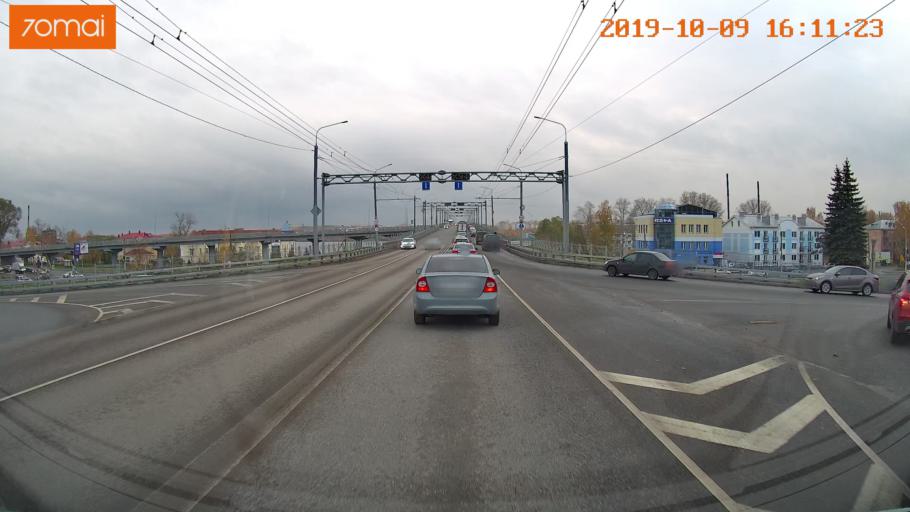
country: RU
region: Kostroma
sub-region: Kostromskoy Rayon
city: Kostroma
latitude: 57.7575
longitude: 40.9460
